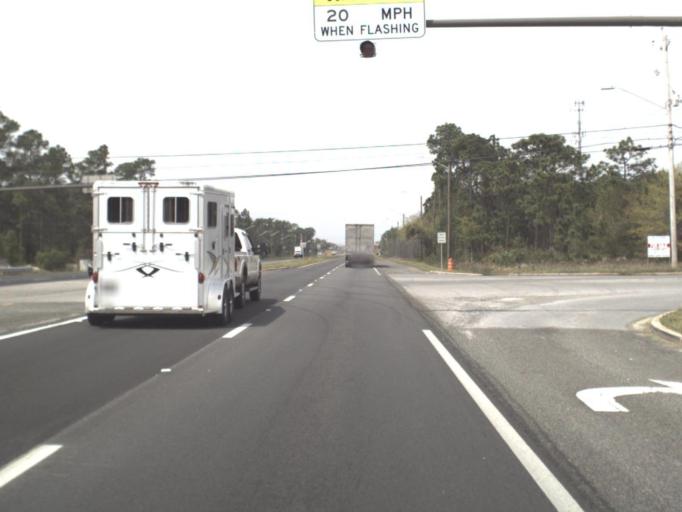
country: US
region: Florida
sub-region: Santa Rosa County
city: Holley
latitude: 30.4021
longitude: -86.9187
